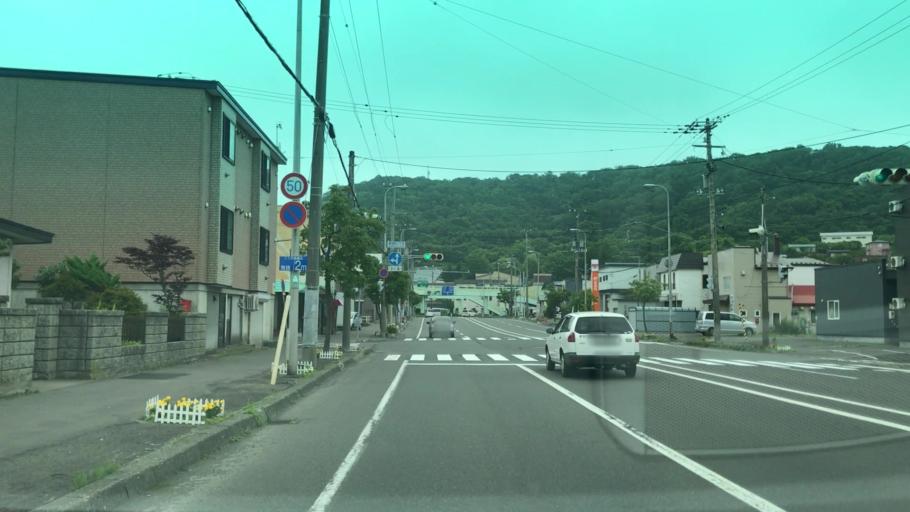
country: JP
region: Hokkaido
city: Muroran
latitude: 42.3564
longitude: 141.0466
